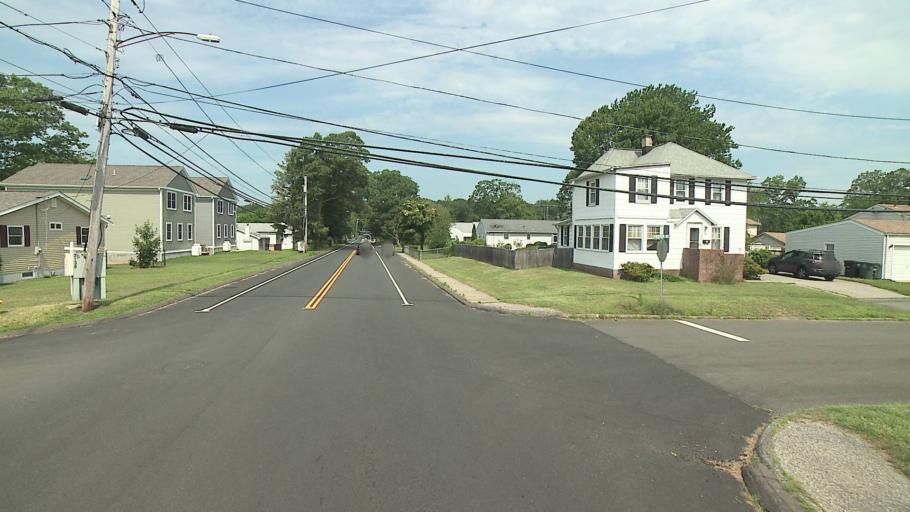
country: US
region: Connecticut
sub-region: New Haven County
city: Milford
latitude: 41.2106
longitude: -73.0262
